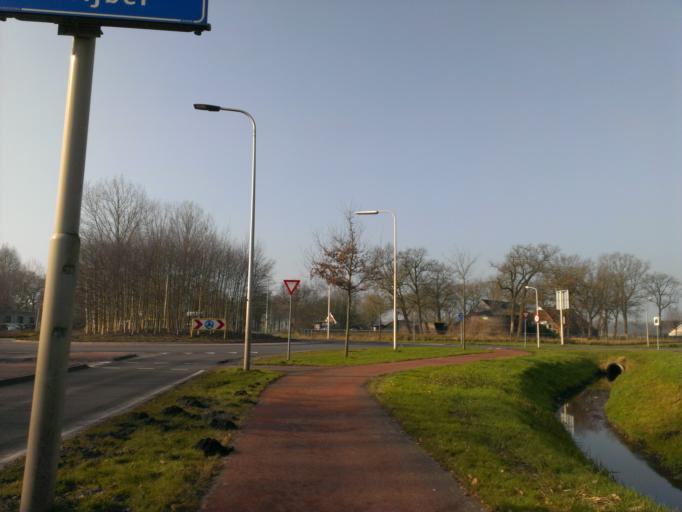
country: NL
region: Drenthe
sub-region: Gemeente Hoogeveen
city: Hoogeveen
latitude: 52.7384
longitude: 6.4907
